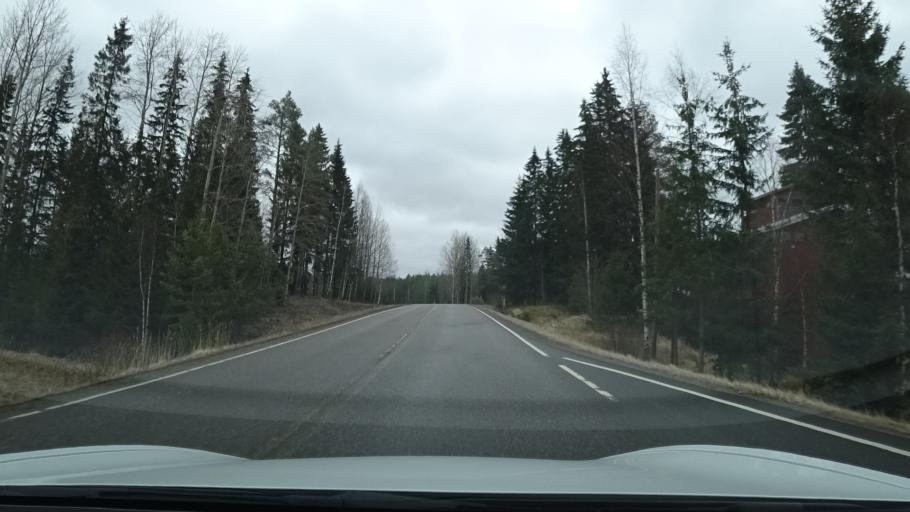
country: FI
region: Uusimaa
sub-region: Helsinki
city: Pornainen
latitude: 60.4877
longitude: 25.4538
